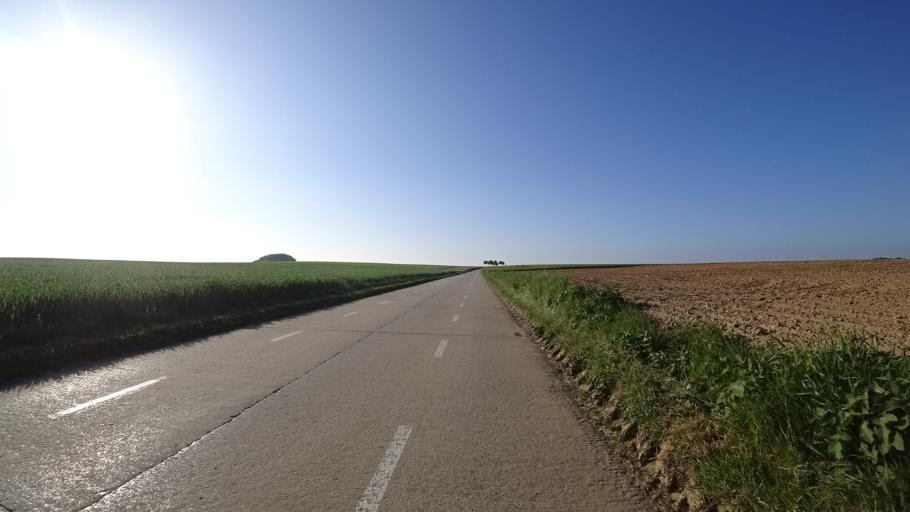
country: BE
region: Wallonia
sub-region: Province du Brabant Wallon
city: Walhain-Saint-Paul
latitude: 50.6307
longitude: 4.6844
